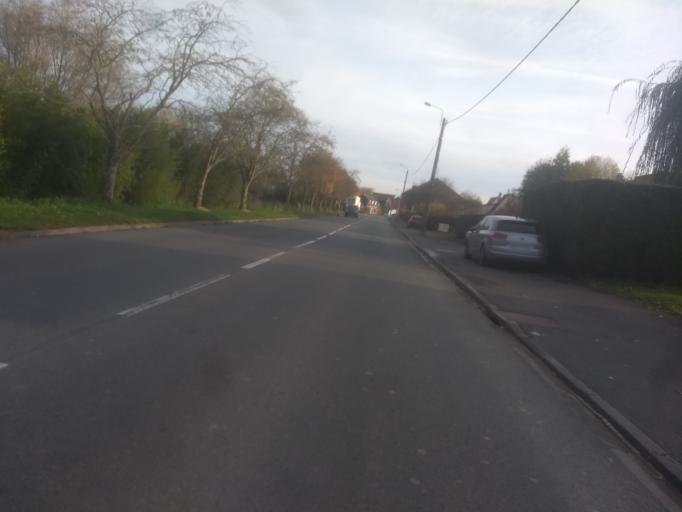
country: FR
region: Nord-Pas-de-Calais
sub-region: Departement du Pas-de-Calais
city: Agny
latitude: 50.2628
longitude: 2.7558
